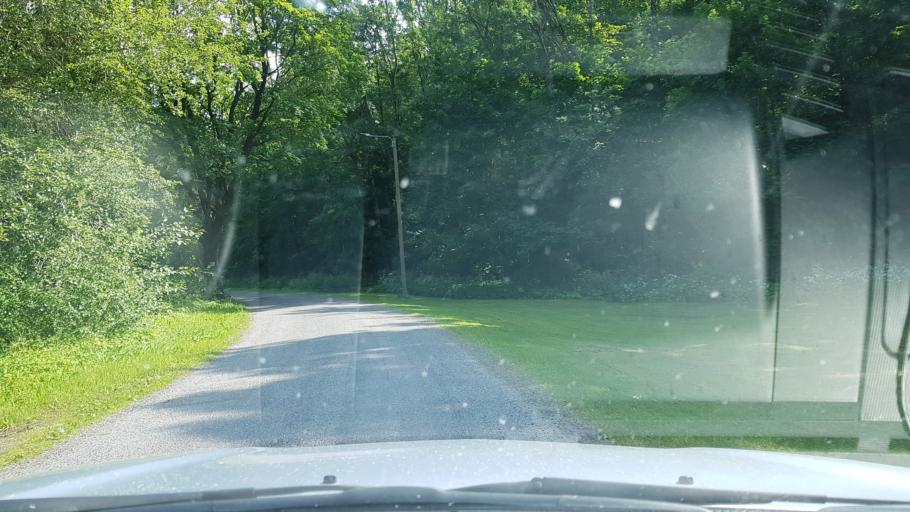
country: EE
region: Ida-Virumaa
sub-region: Sillamaee linn
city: Sillamae
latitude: 59.3745
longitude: 27.8811
